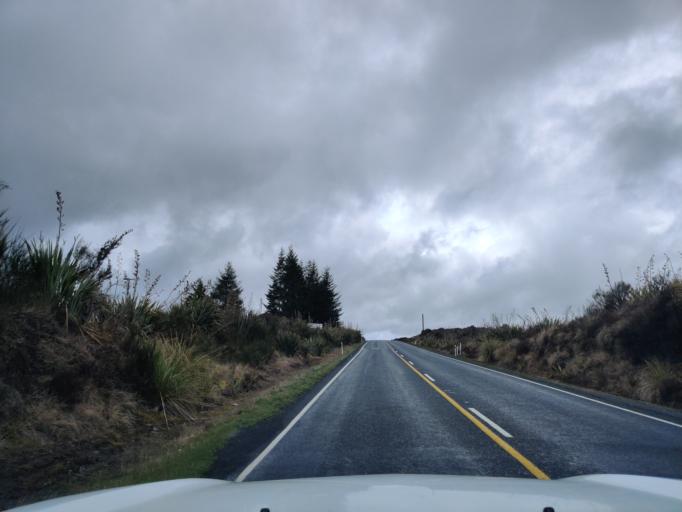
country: NZ
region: Manawatu-Wanganui
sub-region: Ruapehu District
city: Waiouru
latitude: -39.1986
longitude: 175.4013
